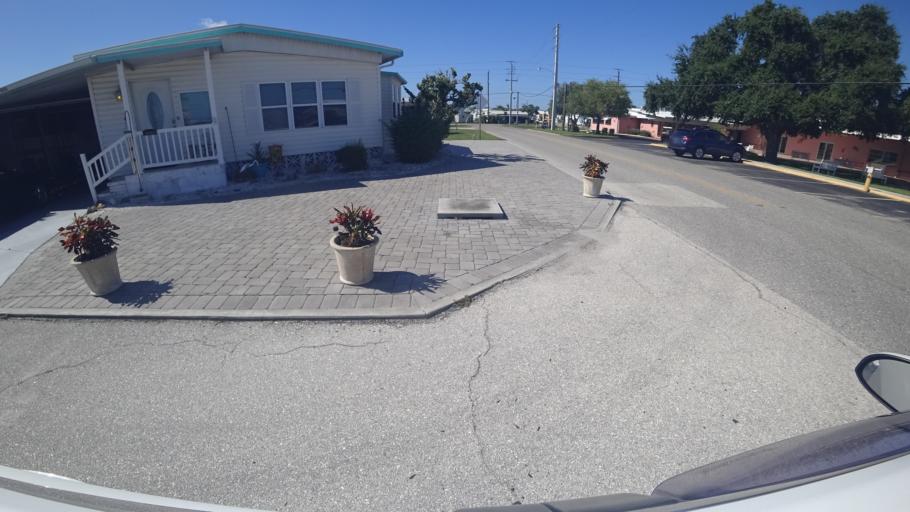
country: US
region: Florida
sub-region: Manatee County
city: Bayshore Gardens
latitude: 27.4192
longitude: -82.5805
